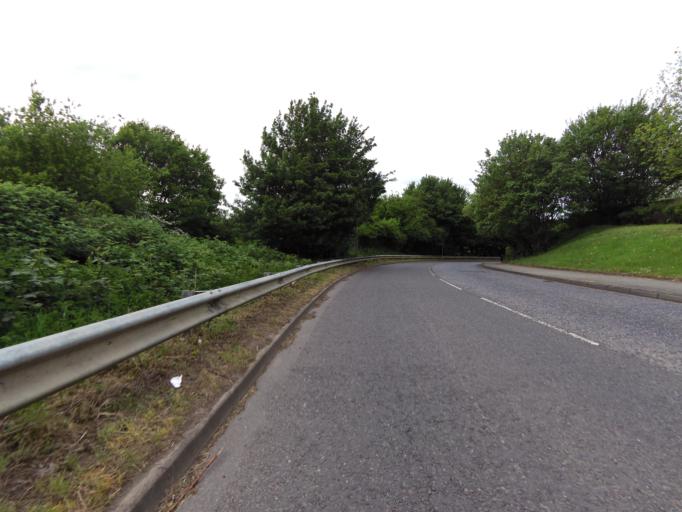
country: GB
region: England
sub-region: Suffolk
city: Ipswich
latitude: 52.0385
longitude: 1.1660
